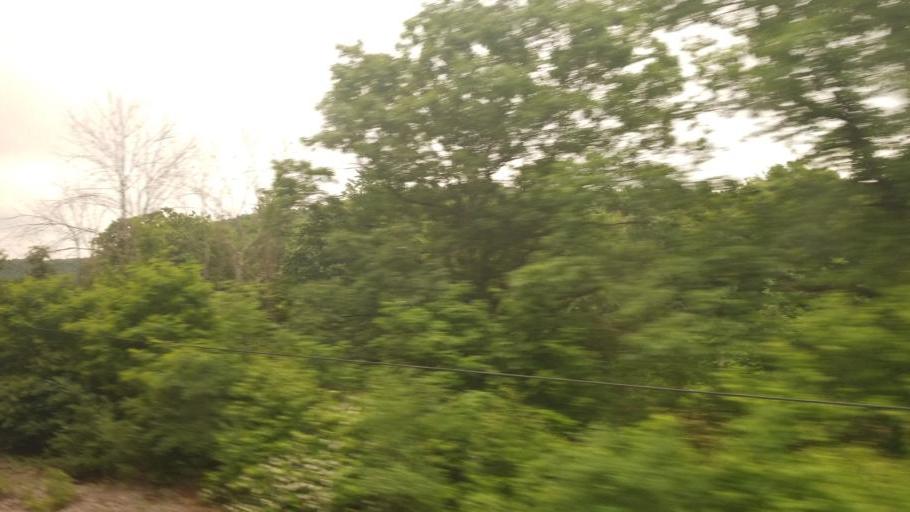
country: US
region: Pennsylvania
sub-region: Somerset County
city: Milford
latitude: 39.8963
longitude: -79.2061
